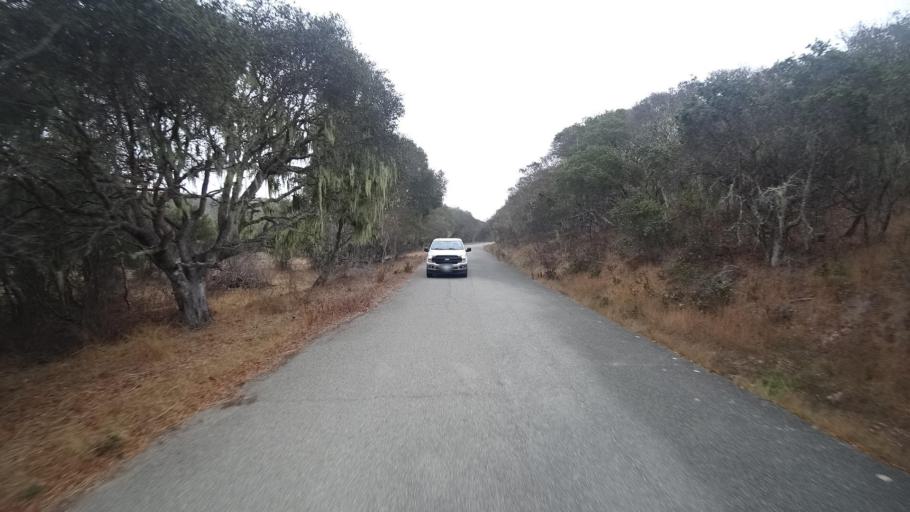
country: US
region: California
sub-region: Monterey County
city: Marina
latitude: 36.6514
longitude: -121.7493
